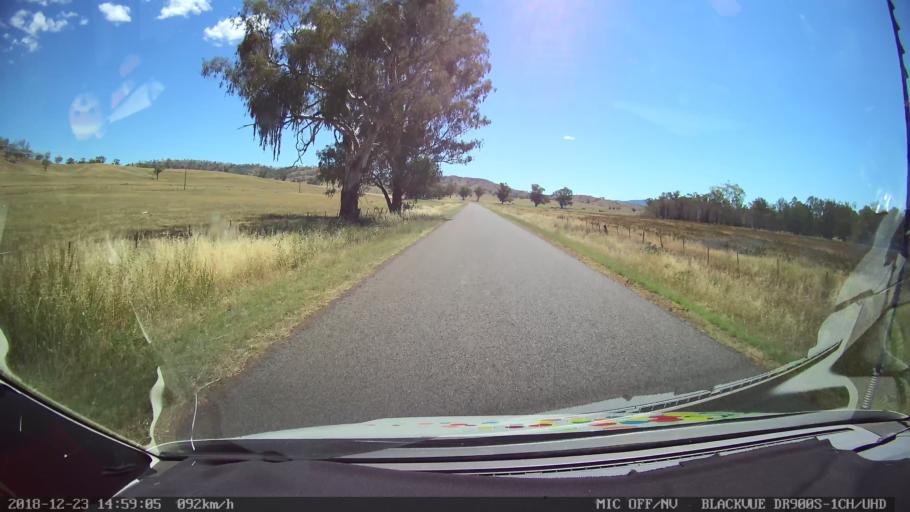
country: AU
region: New South Wales
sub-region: Tamworth Municipality
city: Manilla
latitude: -30.7214
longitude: 150.8056
